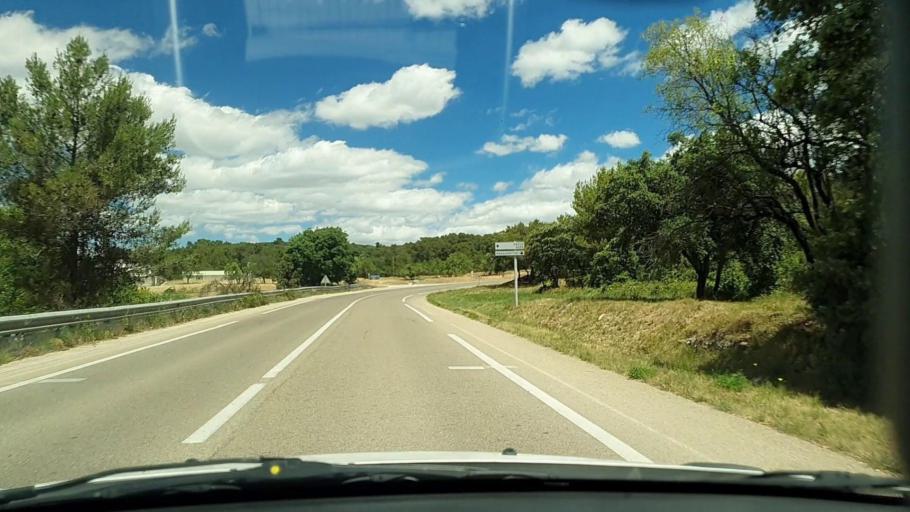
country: FR
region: Languedoc-Roussillon
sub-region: Departement du Gard
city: Poulx
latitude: 43.8903
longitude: 4.4172
